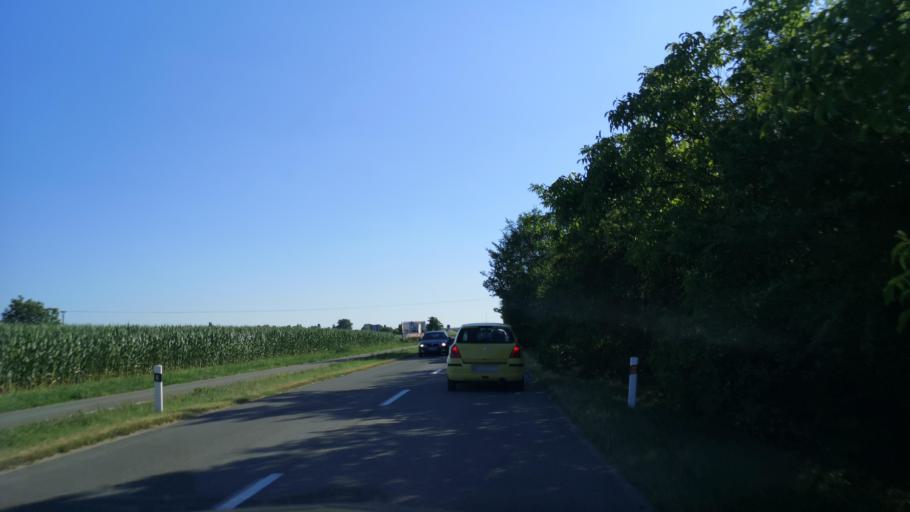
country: SK
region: Trnavsky
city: Dunajska Streda
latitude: 48.0330
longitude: 17.5461
